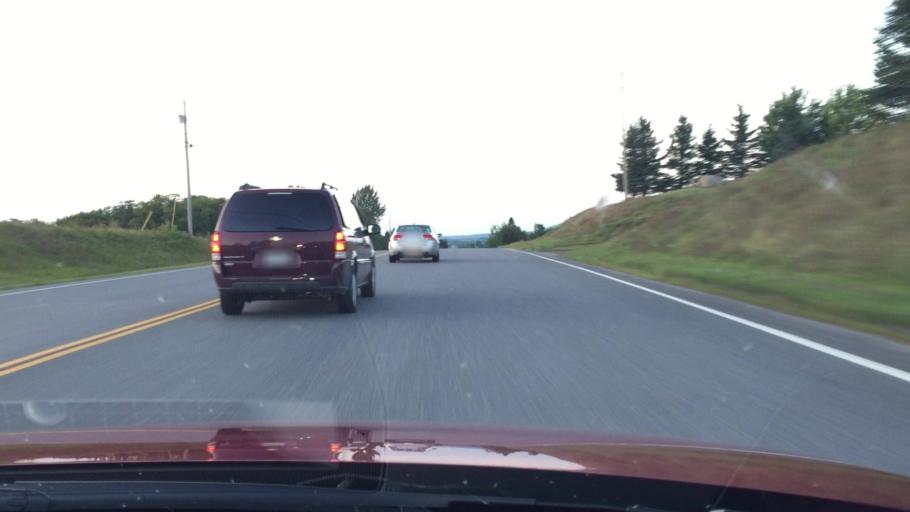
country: CA
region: New Brunswick
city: Florenceville-Bristol
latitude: 46.3914
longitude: -67.8428
